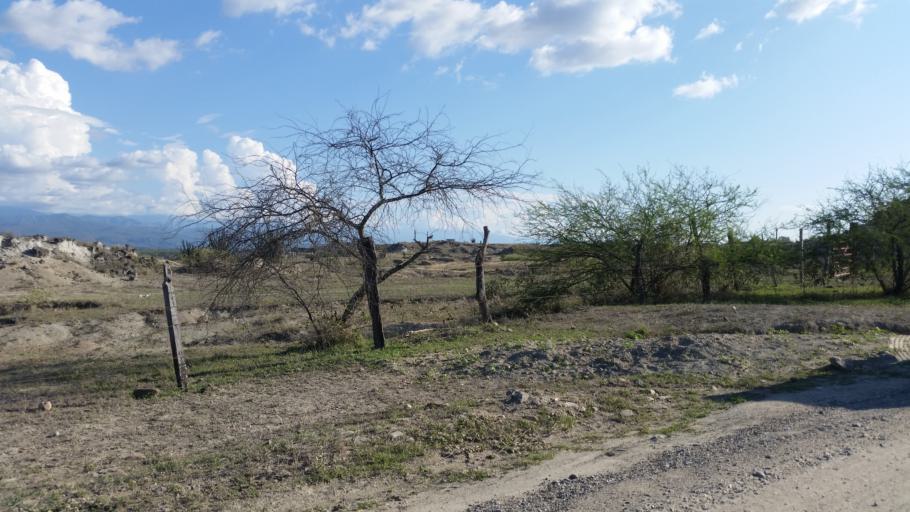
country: CO
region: Huila
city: Villavieja
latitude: 3.2245
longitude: -75.1267
